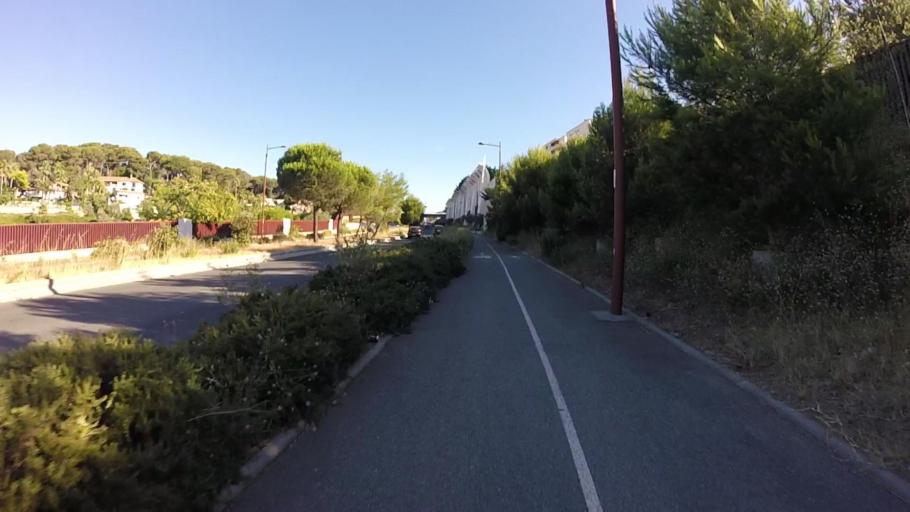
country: FR
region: Provence-Alpes-Cote d'Azur
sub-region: Departement des Alpes-Maritimes
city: Biot
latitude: 43.5915
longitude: 7.0923
